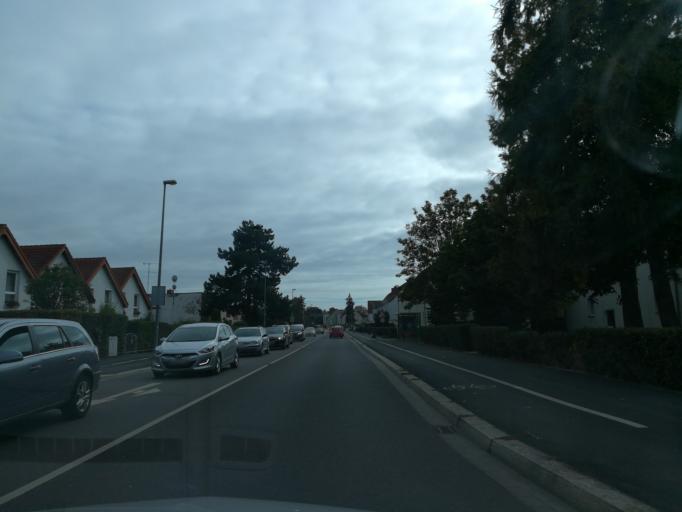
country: DE
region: Saxony-Anhalt
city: Neue Neustadt
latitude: 52.1499
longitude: 11.6075
